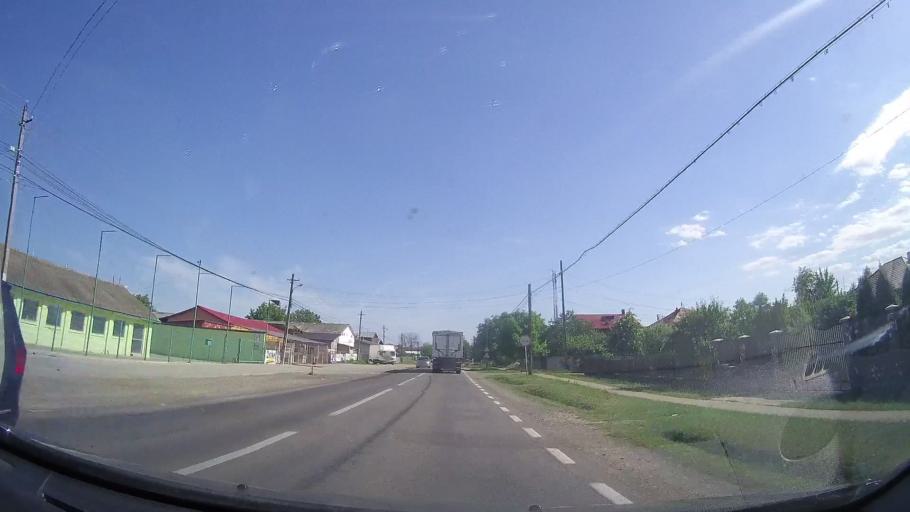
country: RO
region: Prahova
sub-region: Comuna Magurele
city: Magurele
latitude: 45.1018
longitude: 26.0357
